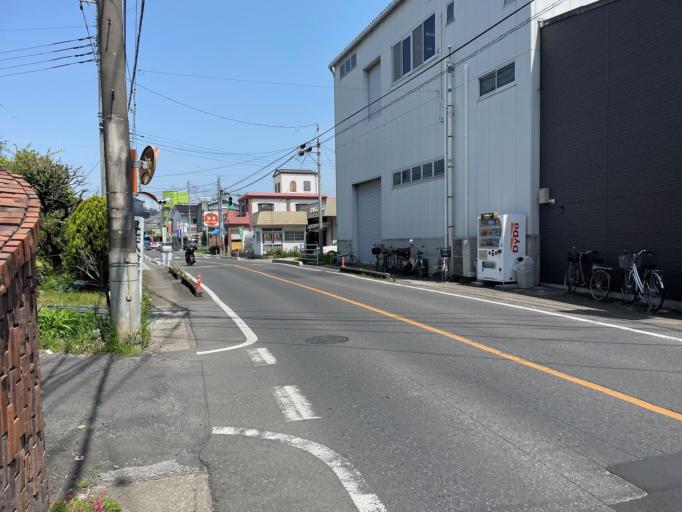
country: JP
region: Tochigi
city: Ashikaga
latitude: 36.3076
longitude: 139.4533
